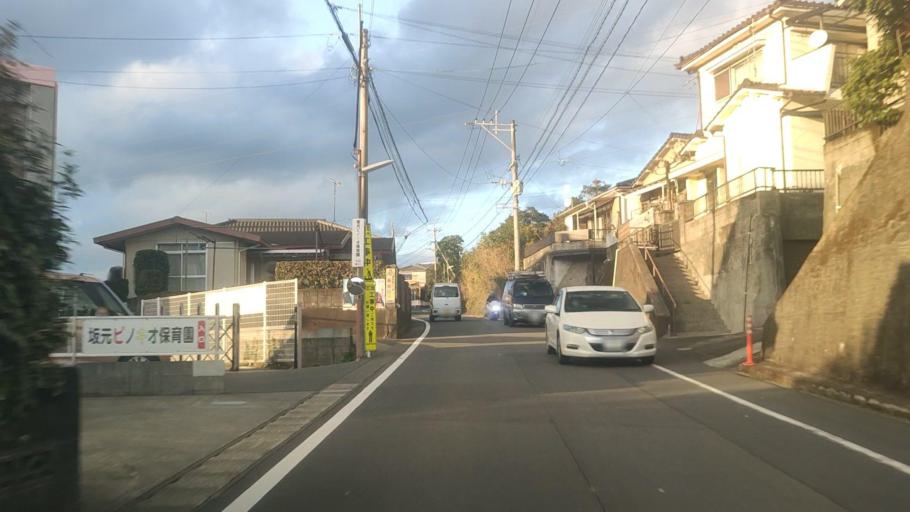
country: JP
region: Kagoshima
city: Kagoshima-shi
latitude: 31.6228
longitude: 130.5529
